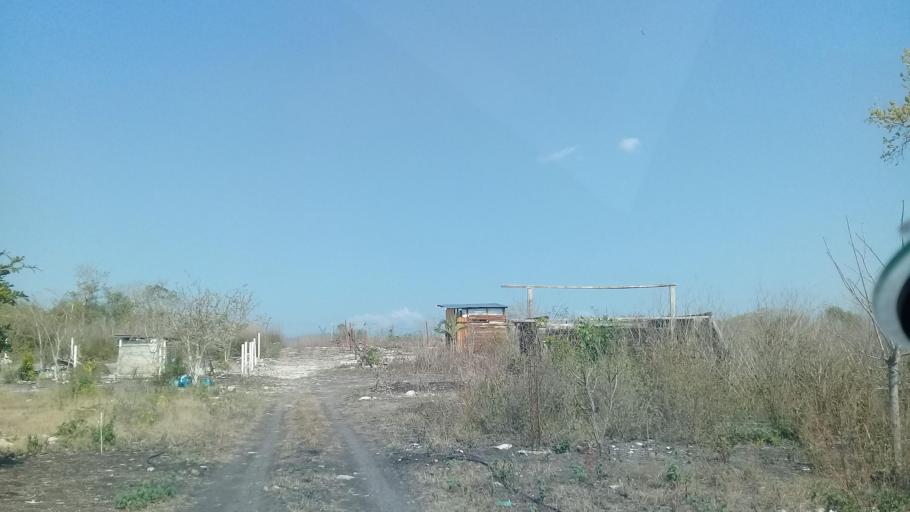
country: MX
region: Veracruz
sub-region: Emiliano Zapata
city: Plan del Rio
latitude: 19.4022
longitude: -96.6152
